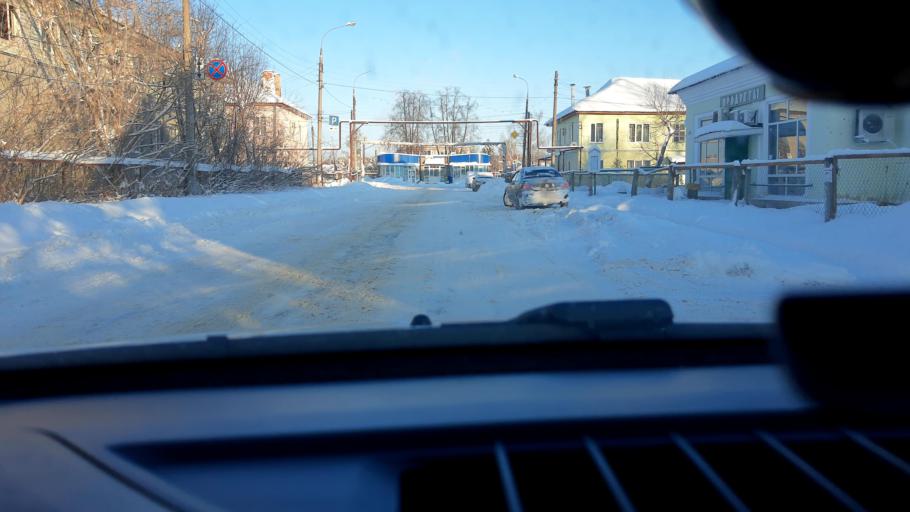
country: RU
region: Nizjnij Novgorod
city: Lukino
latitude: 56.3375
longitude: 43.6177
